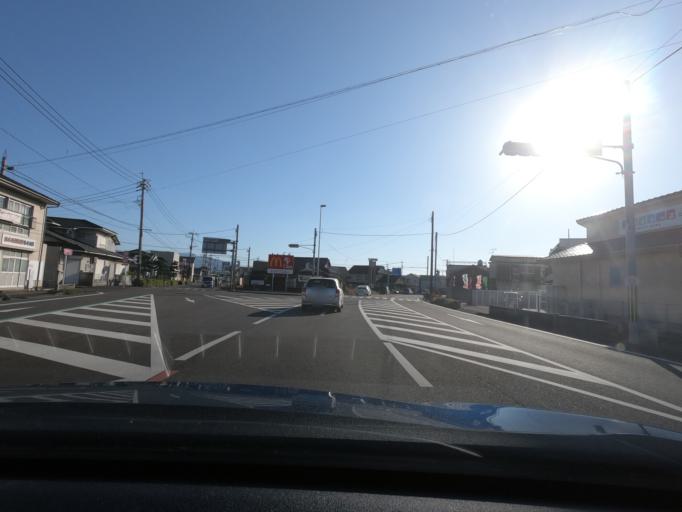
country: JP
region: Kagoshima
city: Izumi
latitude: 32.1173
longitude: 130.3400
